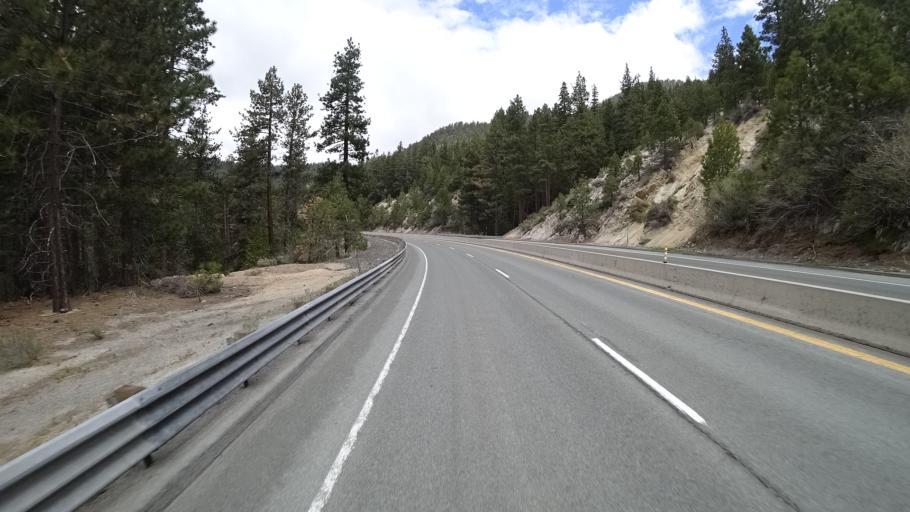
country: US
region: Nevada
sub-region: Douglas County
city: Indian Hills
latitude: 39.1185
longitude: -119.8721
